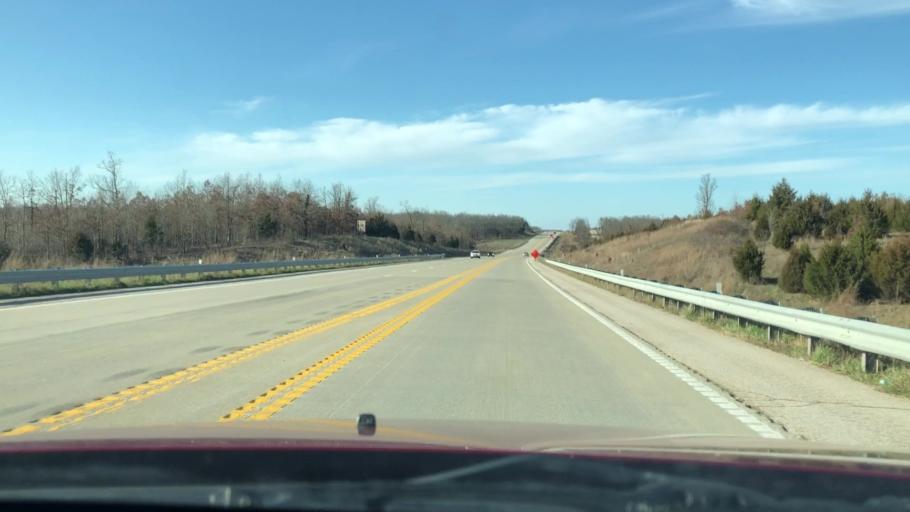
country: US
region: Missouri
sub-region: Camden County
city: Camdenton
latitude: 37.9404
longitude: -92.7156
